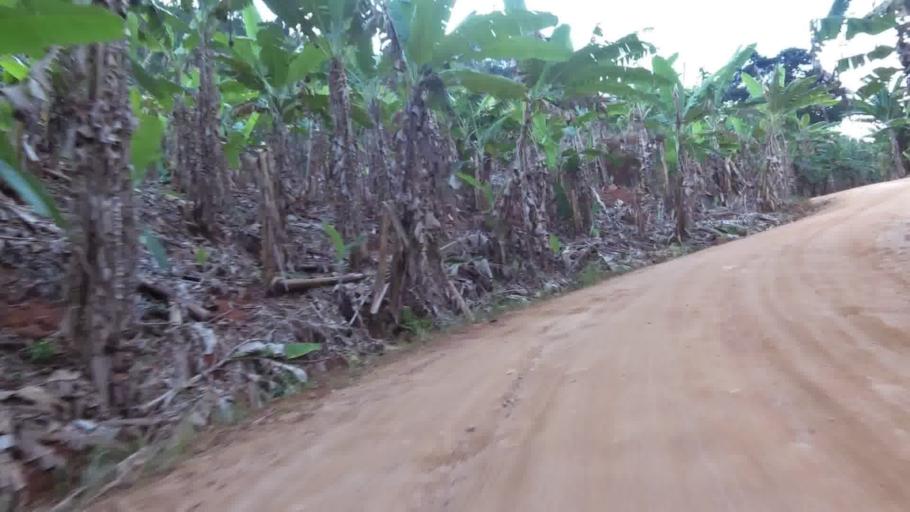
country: BR
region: Espirito Santo
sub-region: Alfredo Chaves
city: Alfredo Chaves
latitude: -20.5621
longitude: -40.6932
